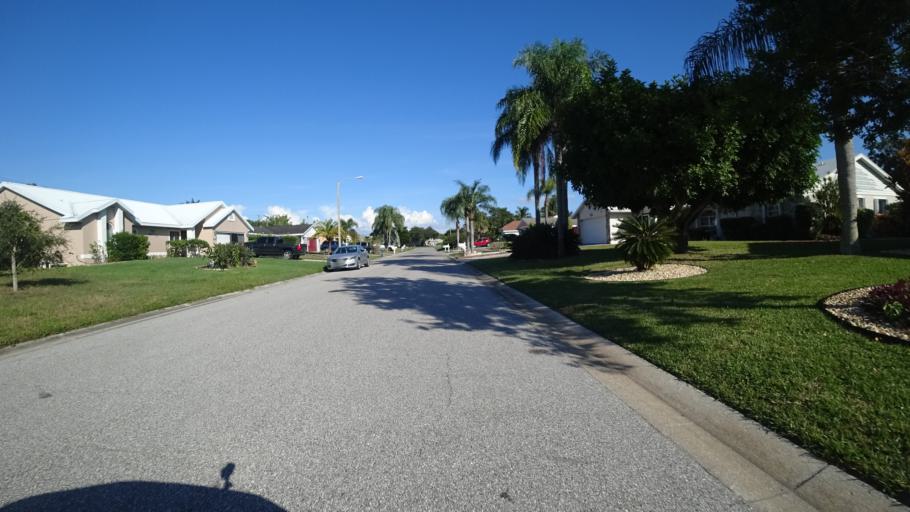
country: US
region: Florida
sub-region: Manatee County
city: West Bradenton
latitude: 27.4733
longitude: -82.6271
